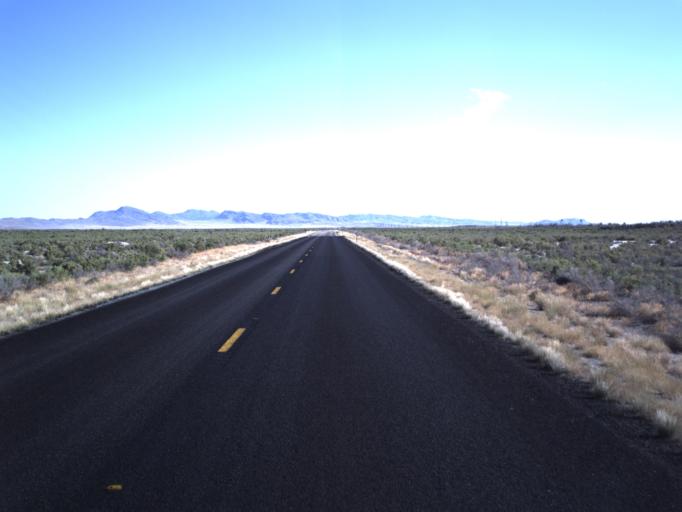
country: US
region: Utah
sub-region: Beaver County
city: Milford
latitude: 38.5943
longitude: -112.9879
